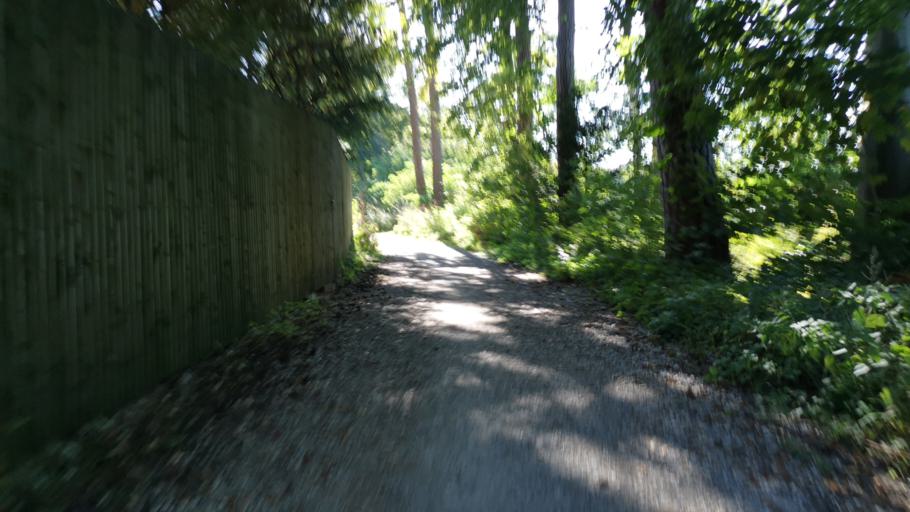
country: DE
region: Bavaria
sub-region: Upper Bavaria
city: Pullach im Isartal
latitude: 48.0582
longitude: 11.5398
